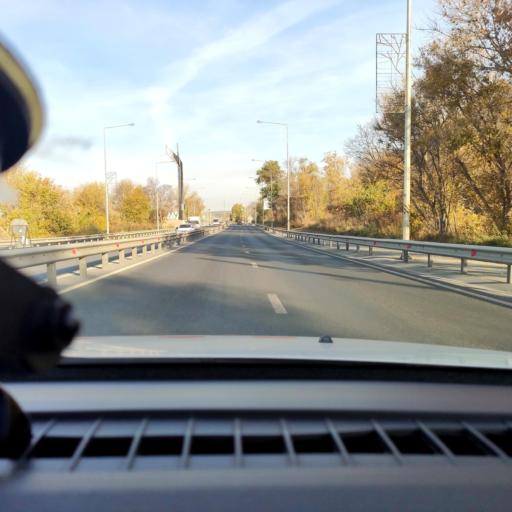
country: RU
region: Samara
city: Volzhskiy
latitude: 53.4053
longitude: 50.1452
